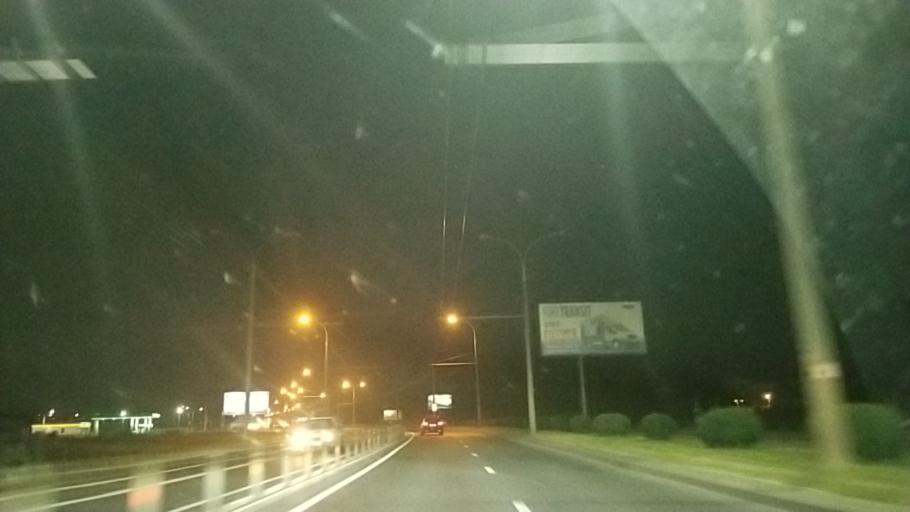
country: BY
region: Brest
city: Brest
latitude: 52.0780
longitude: 23.7692
